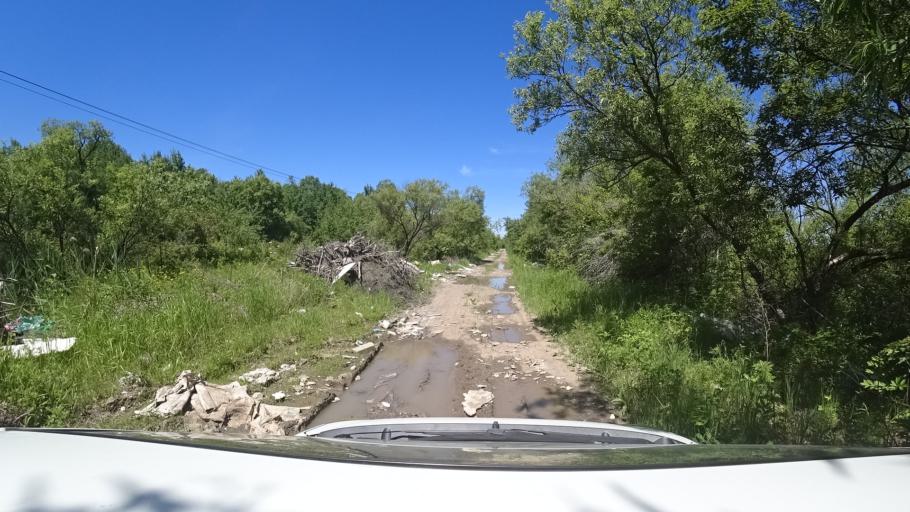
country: RU
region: Khabarovsk Krai
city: Topolevo
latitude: 48.4864
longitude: 135.1766
